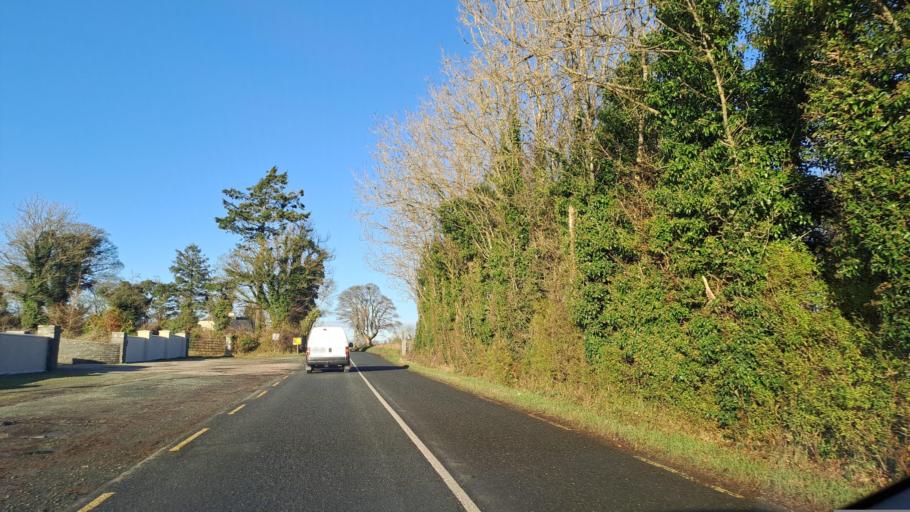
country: IE
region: Ulster
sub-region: An Cabhan
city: Mullagh
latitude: 53.8370
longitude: -6.9537
